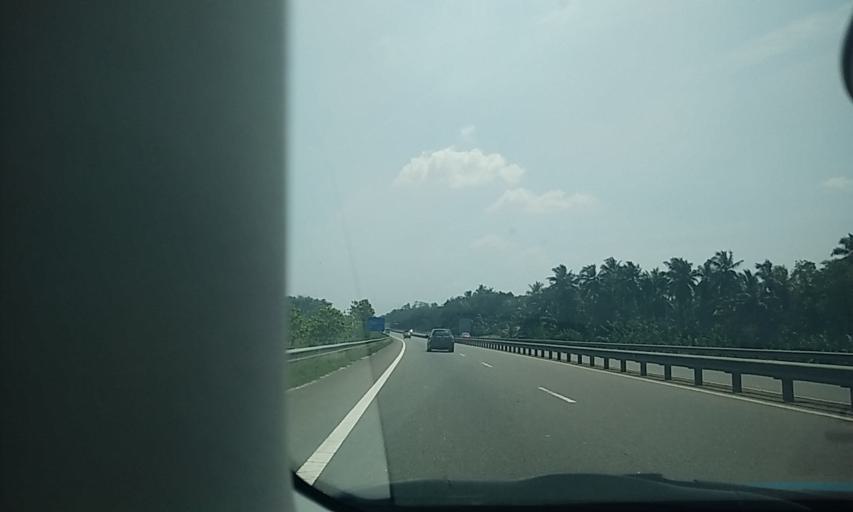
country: LK
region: Western
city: Homagama
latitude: 6.7699
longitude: 79.9827
